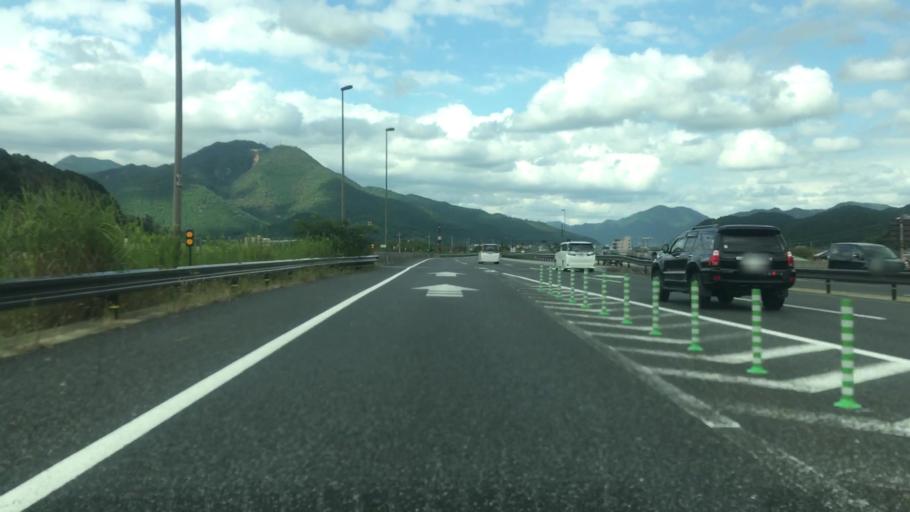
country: JP
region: Kyoto
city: Fukuchiyama
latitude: 35.1647
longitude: 135.0446
